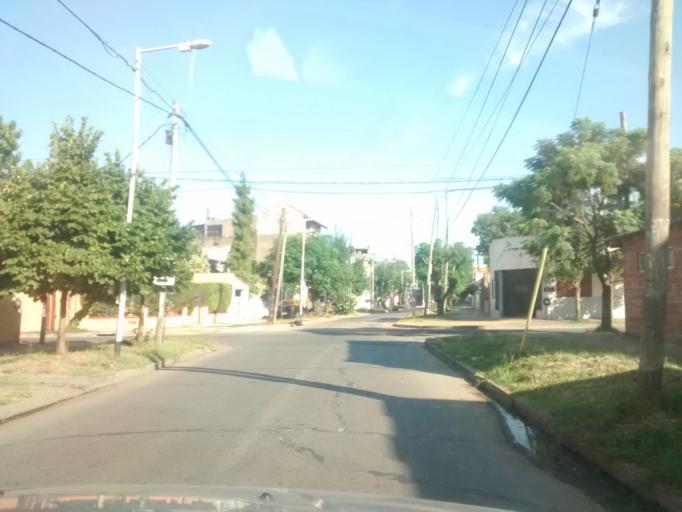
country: AR
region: Buenos Aires
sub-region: Partido de Avellaneda
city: Avellaneda
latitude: -34.6847
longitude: -58.3504
